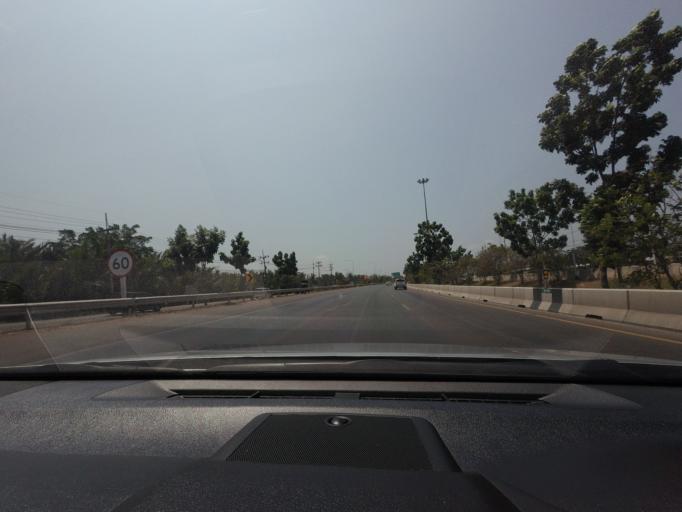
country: TH
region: Samut Songkhram
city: Samut Songkhram
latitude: 13.3843
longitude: 99.9916
